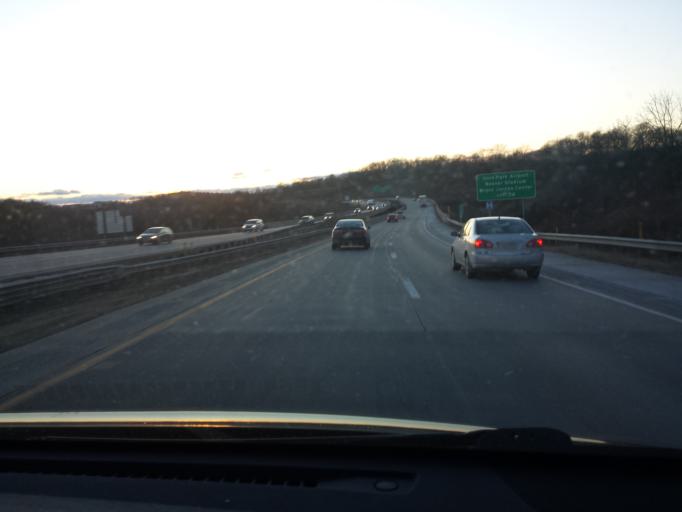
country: US
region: Pennsylvania
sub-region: Centre County
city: Houserville
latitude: 40.8438
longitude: -77.8201
